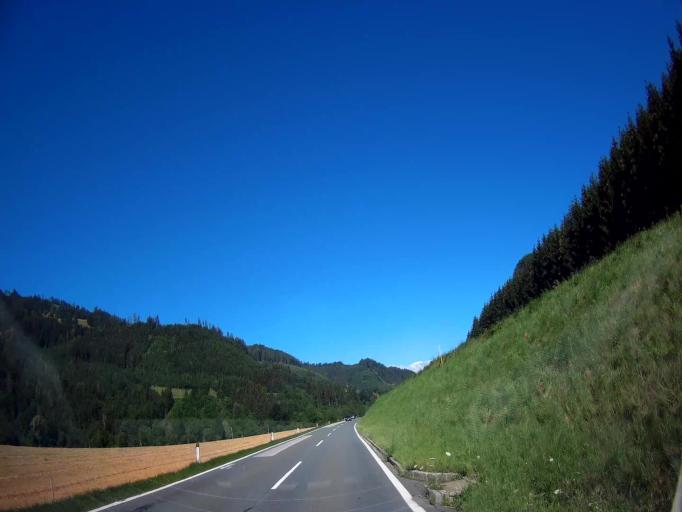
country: AT
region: Carinthia
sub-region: Politischer Bezirk Sankt Veit an der Glan
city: Bruckl
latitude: 46.7481
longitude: 14.5153
